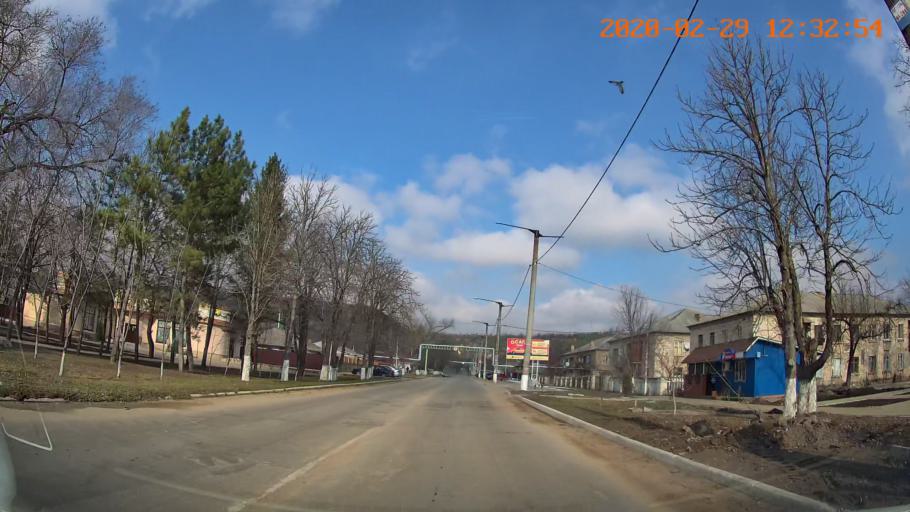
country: MD
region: Telenesti
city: Camenca
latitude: 48.0316
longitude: 28.7031
